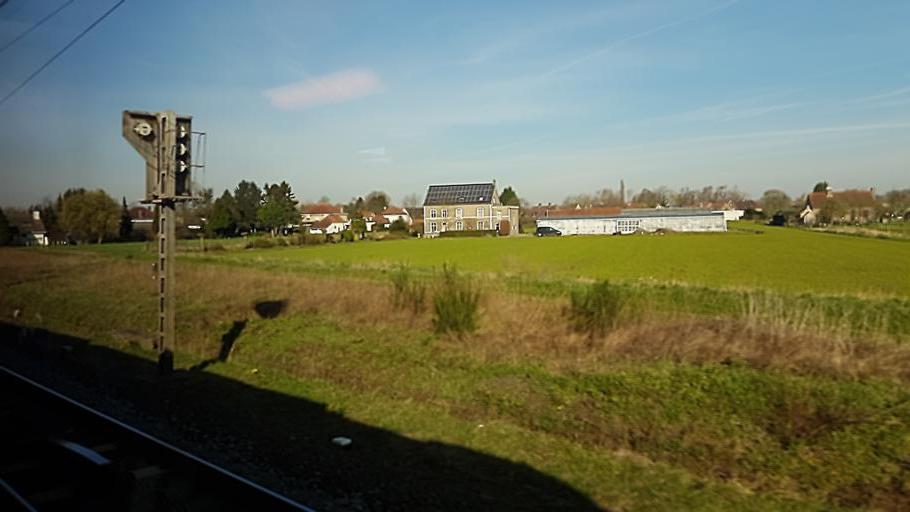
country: BE
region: Flanders
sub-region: Provincie Oost-Vlaanderen
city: Sint-Martens-Latem
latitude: 50.9902
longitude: 3.6115
